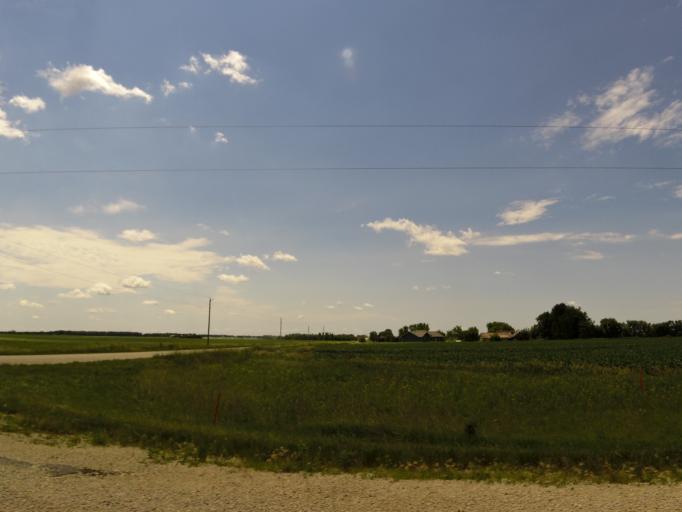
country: US
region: Iowa
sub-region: Buchanan County
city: Fairbank
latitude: 42.7149
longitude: -92.0610
